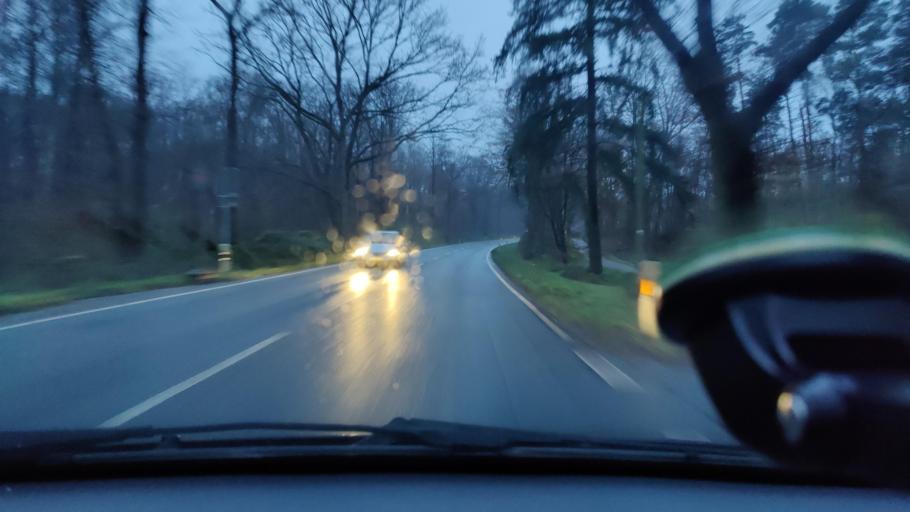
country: DE
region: North Rhine-Westphalia
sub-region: Regierungsbezirk Dusseldorf
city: Sonsbeck
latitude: 51.5939
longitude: 6.3856
